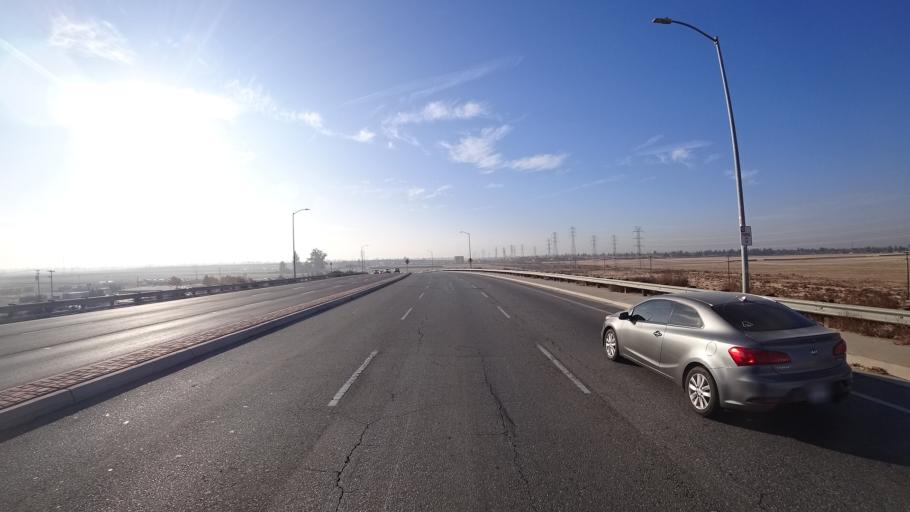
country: US
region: California
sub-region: Kern County
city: Greenacres
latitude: 35.3759
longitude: -119.0938
